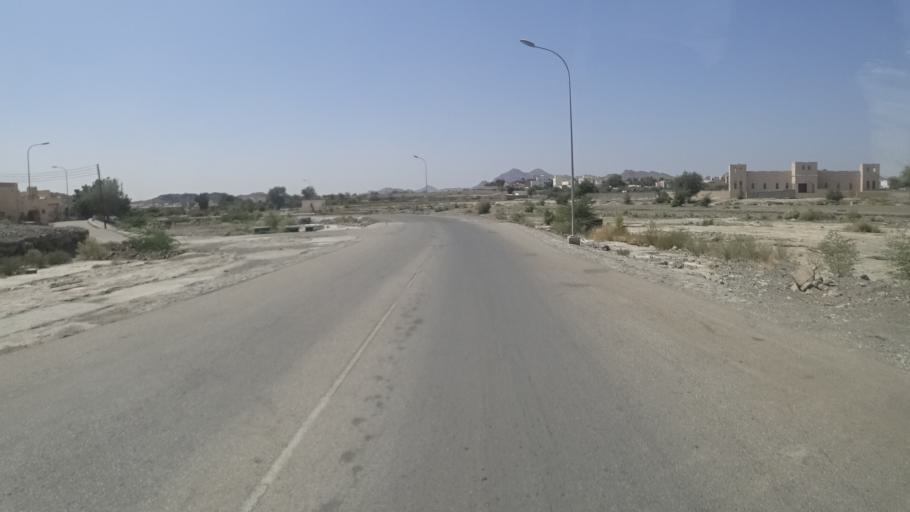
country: OM
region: Ash Sharqiyah
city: Ibra'
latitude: 22.6810
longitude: 58.5363
